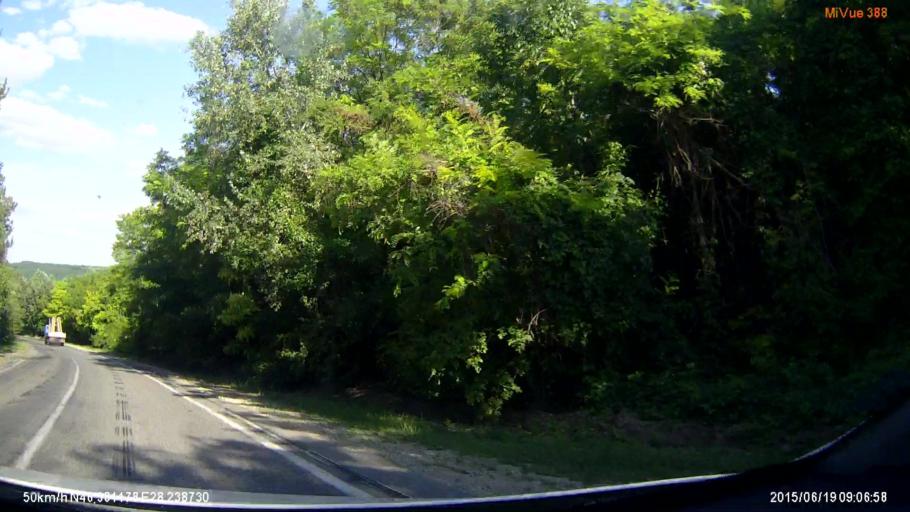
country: RO
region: Vaslui
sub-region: Comuna Vetrisoaia
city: Vetrisoaia
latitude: 46.3812
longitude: 28.2385
